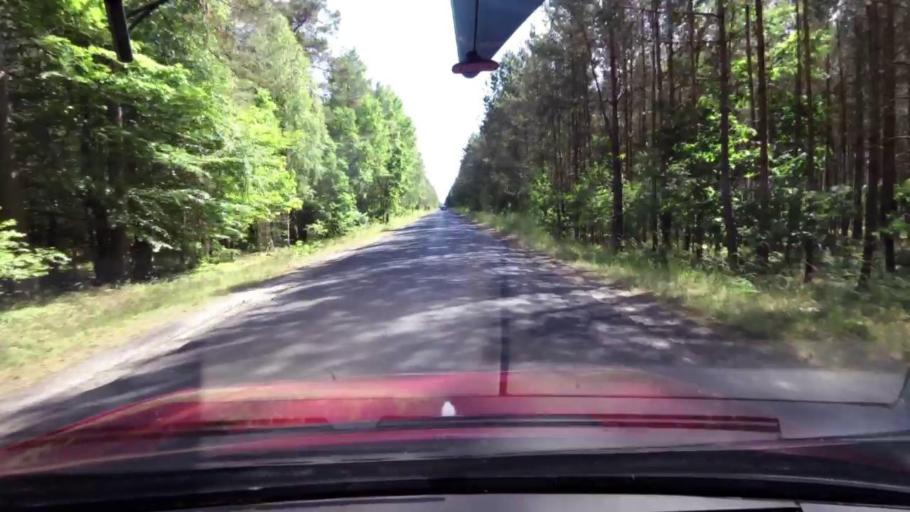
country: PL
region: Pomeranian Voivodeship
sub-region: Powiat slupski
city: Kepice
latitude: 54.3062
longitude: 16.9621
